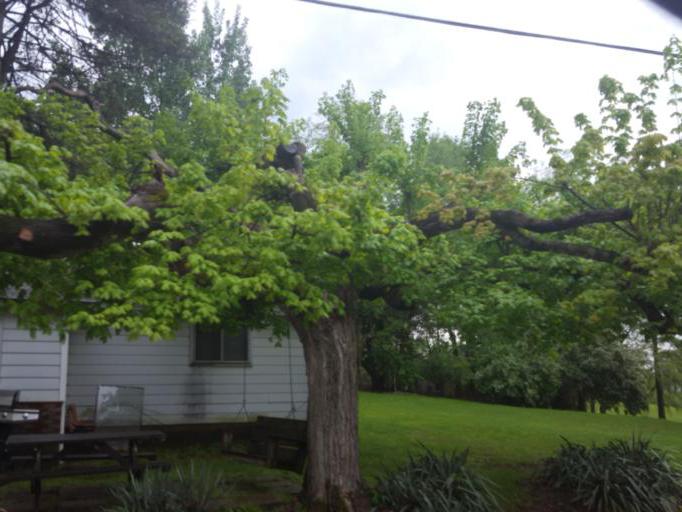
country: US
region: Ohio
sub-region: Fairfield County
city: Millersport
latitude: 39.8988
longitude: -82.5301
